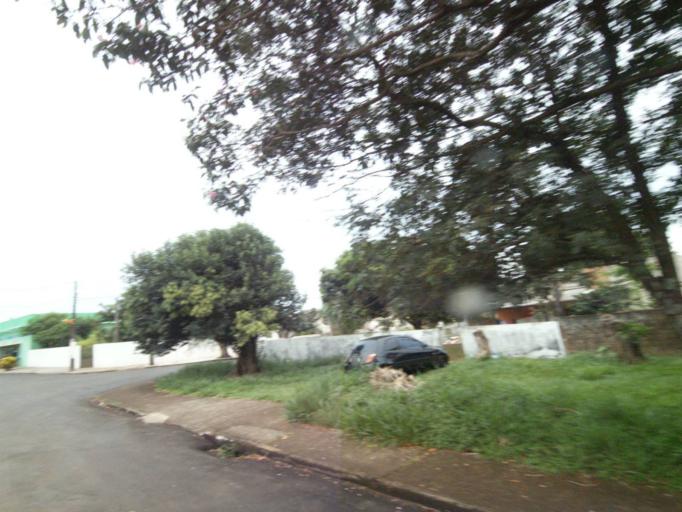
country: BR
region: Parana
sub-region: Campo Mourao
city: Campo Mourao
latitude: -24.0291
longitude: -52.3573
